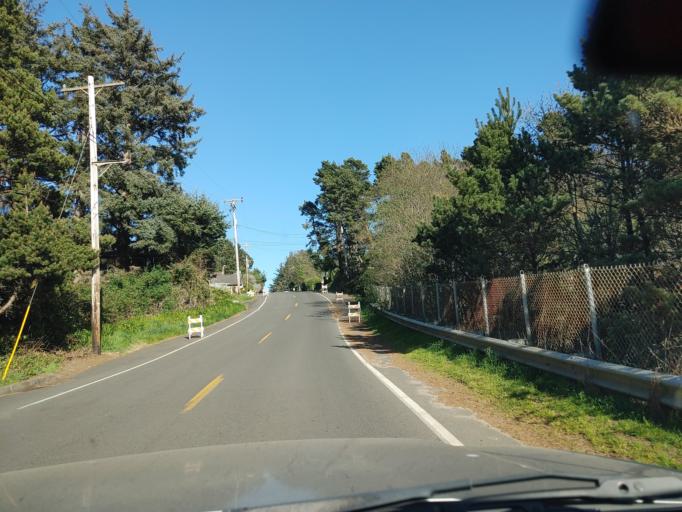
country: US
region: Oregon
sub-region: Lincoln County
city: Depoe Bay
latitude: 44.7472
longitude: -124.0622
